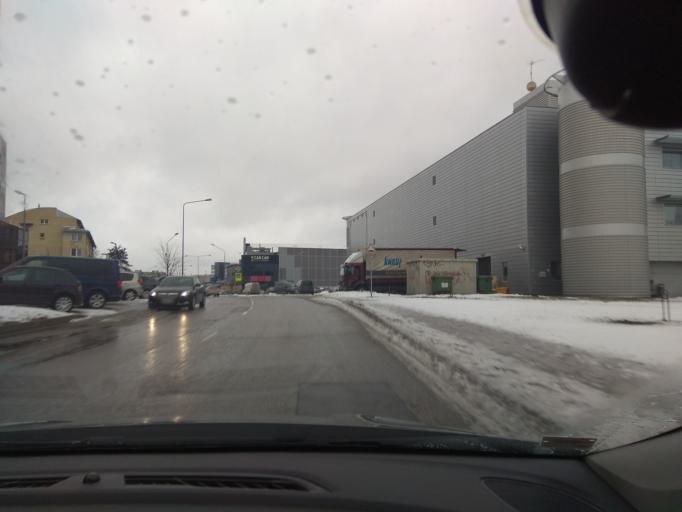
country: LT
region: Vilnius County
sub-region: Vilnius
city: Fabijoniskes
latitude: 54.7262
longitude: 25.2395
